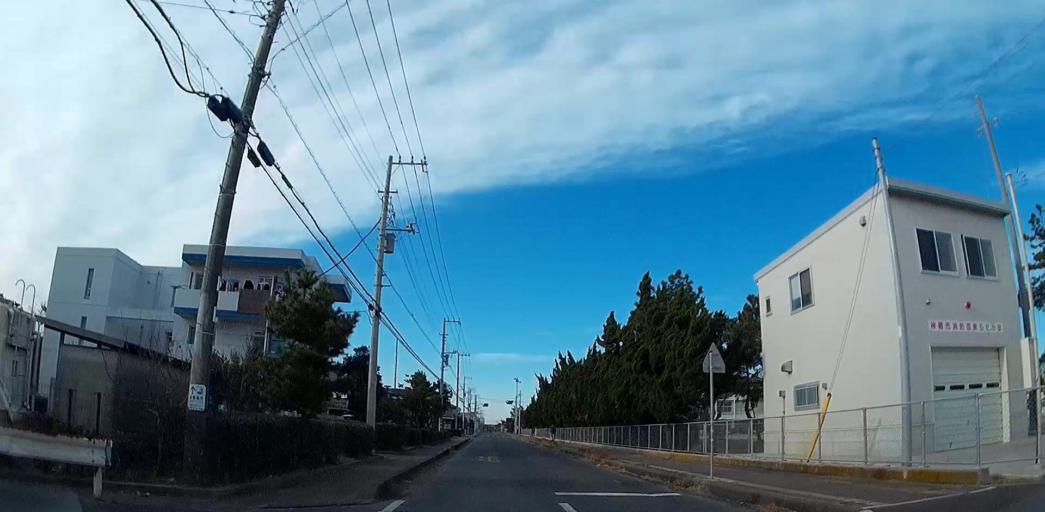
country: JP
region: Chiba
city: Hasaki
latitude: 35.7467
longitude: 140.8352
